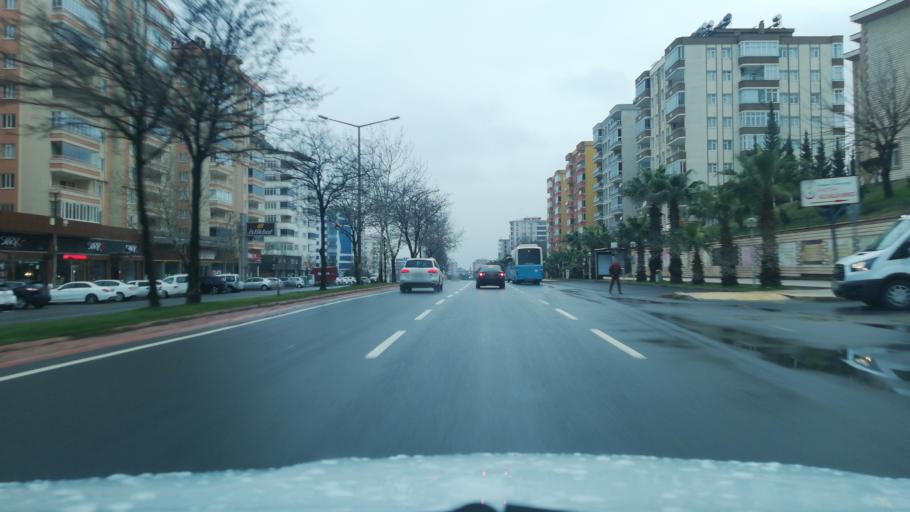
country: TR
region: Kahramanmaras
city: Kahramanmaras
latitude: 37.5925
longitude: 36.8641
